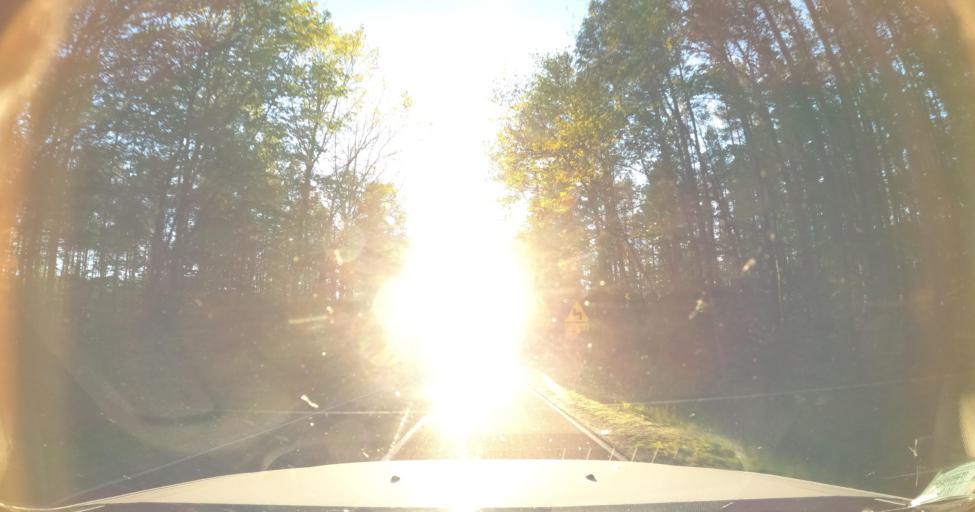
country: PL
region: Pomeranian Voivodeship
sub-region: Powiat slupski
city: Potegowo
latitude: 54.4075
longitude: 17.4444
